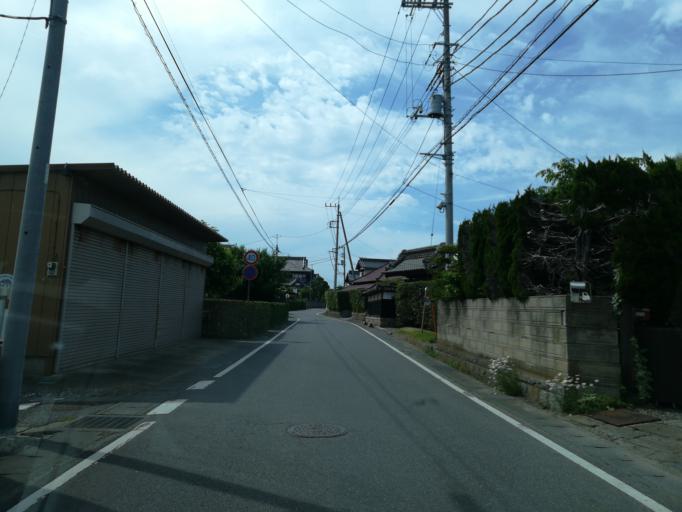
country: JP
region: Ibaraki
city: Tsukuba
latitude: 36.1561
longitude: 140.1088
